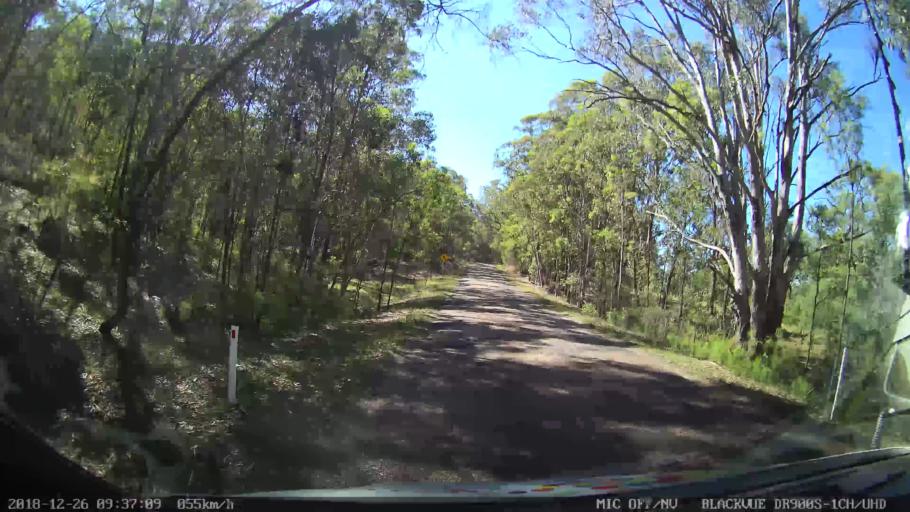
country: AU
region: New South Wales
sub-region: Mid-Western Regional
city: Kandos
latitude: -32.9304
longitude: 150.0390
